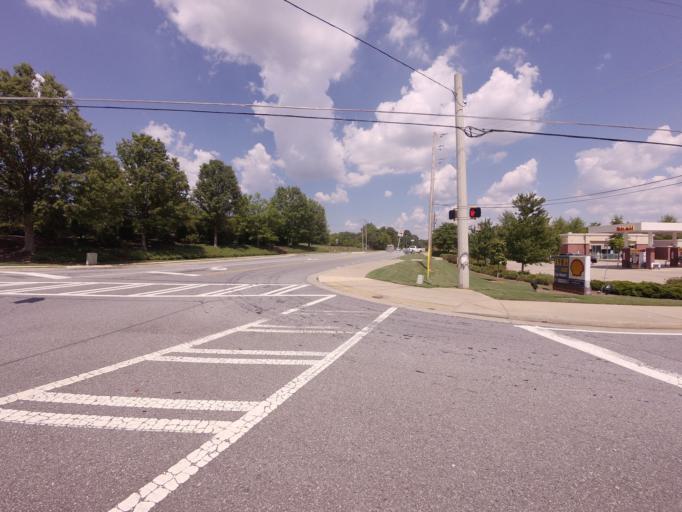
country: US
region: Georgia
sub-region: Fulton County
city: Johns Creek
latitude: 34.0407
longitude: -84.2194
